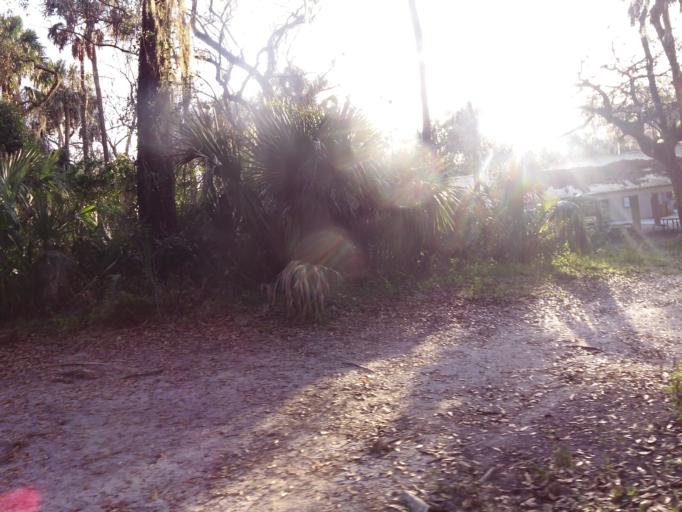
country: US
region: Florida
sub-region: Volusia County
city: Orange City
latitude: 28.9449
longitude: -81.3384
